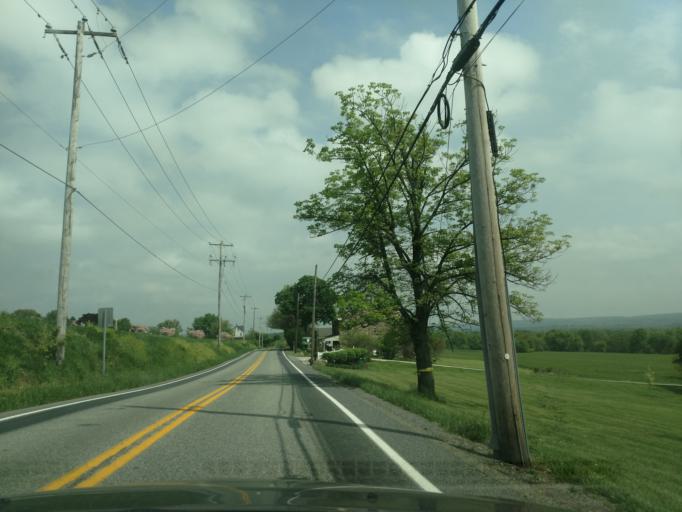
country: US
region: Pennsylvania
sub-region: Chester County
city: Spring City
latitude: 40.1555
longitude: -75.5701
